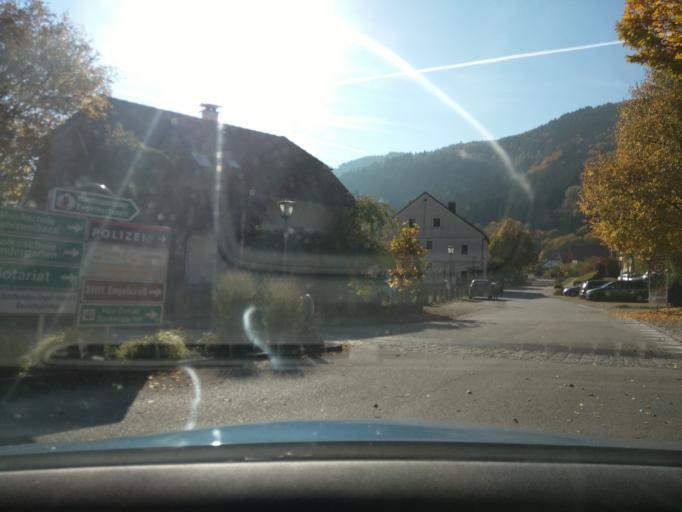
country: AT
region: Upper Austria
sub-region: Politischer Bezirk Rohrbach
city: Pfarrkirchen im Muehlkreis
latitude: 48.5028
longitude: 13.7355
